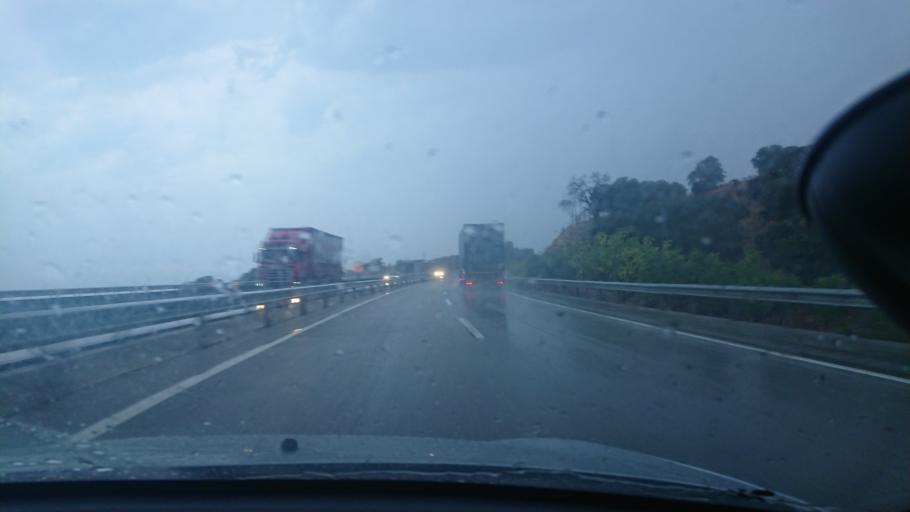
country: TR
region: Manisa
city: Menye
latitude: 38.5304
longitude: 28.4204
